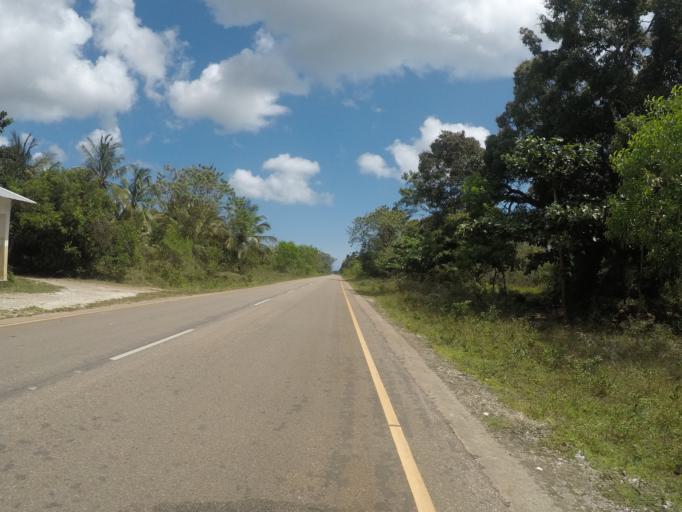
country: TZ
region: Zanzibar Central/South
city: Koani
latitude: -6.2370
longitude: 39.3588
